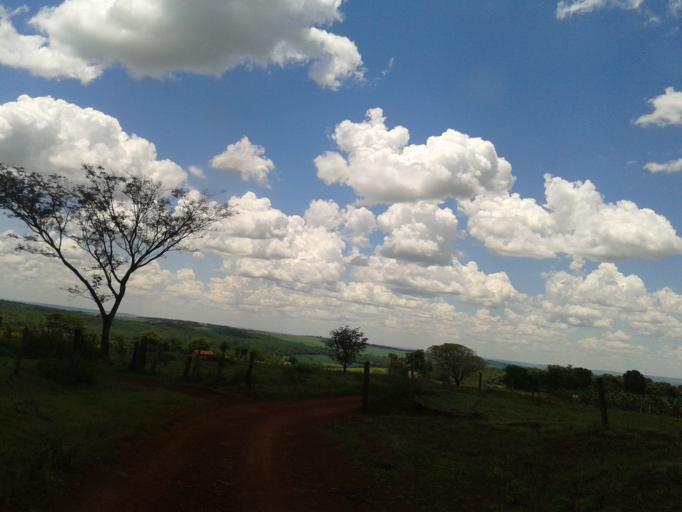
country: BR
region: Minas Gerais
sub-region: Centralina
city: Centralina
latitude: -18.6951
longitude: -49.1936
